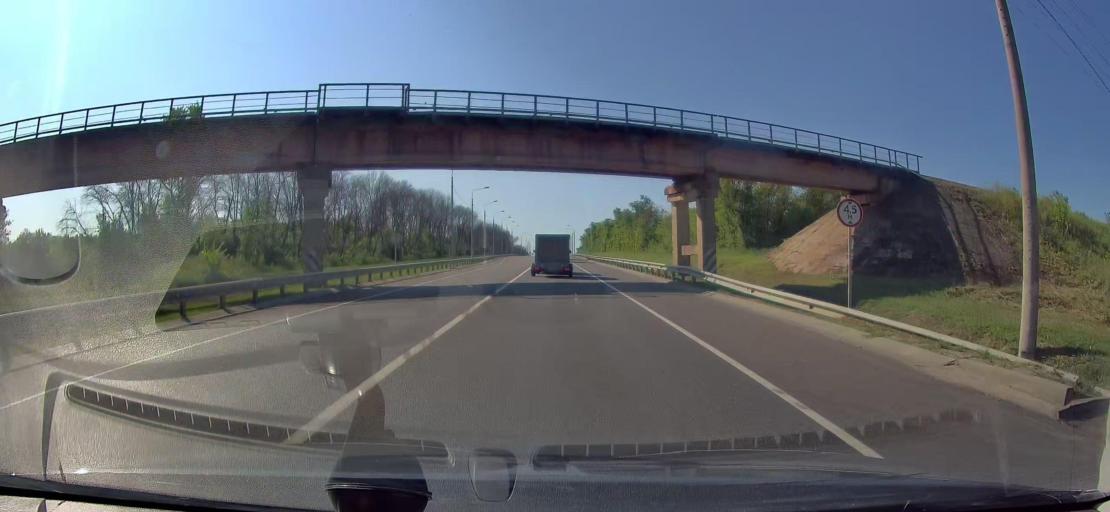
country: RU
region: Orjol
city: Kromy
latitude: 52.6351
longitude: 35.7514
